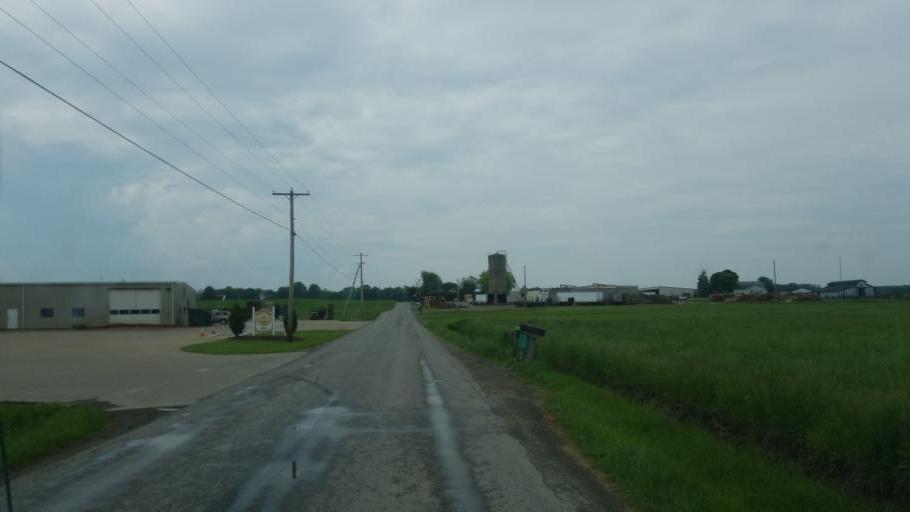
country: US
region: Ohio
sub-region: Wayne County
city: Apple Creek
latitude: 40.7777
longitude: -81.8125
